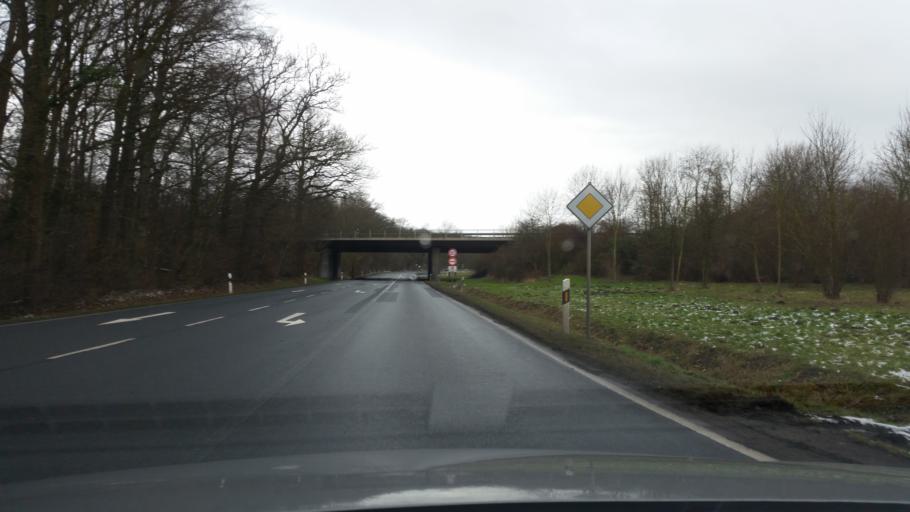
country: DE
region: Lower Saxony
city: Cramme
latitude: 52.1364
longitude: 10.4936
